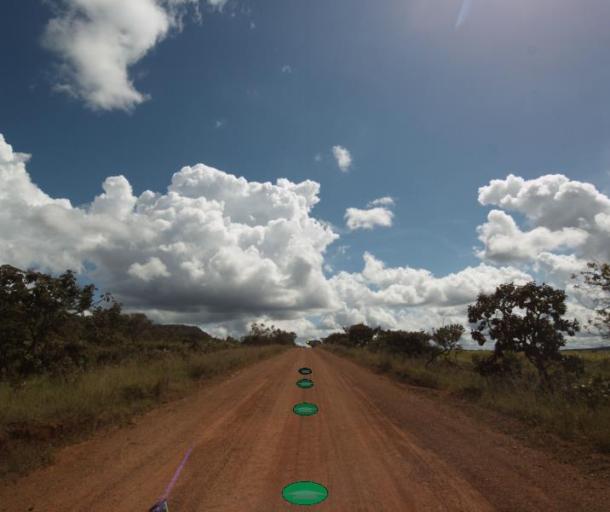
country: BR
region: Goias
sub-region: Pirenopolis
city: Pirenopolis
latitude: -15.7808
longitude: -48.8309
